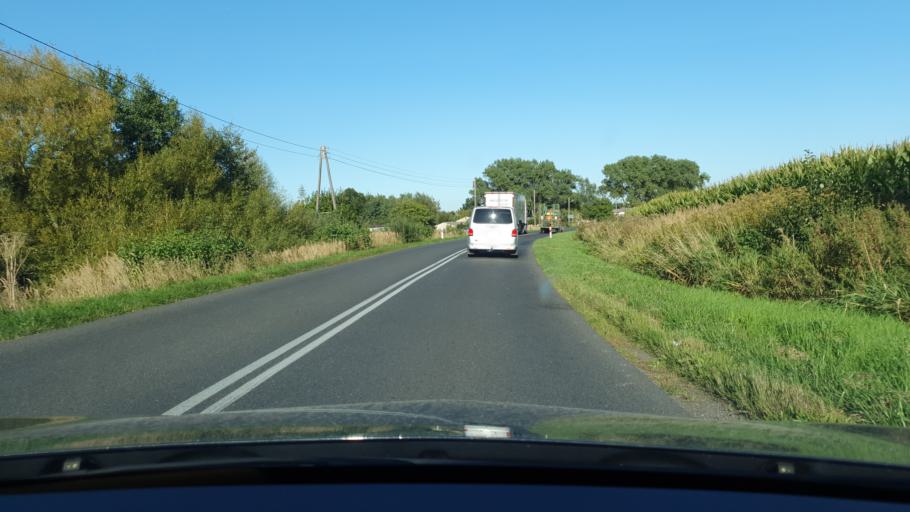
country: PL
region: West Pomeranian Voivodeship
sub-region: Powiat kamienski
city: Golczewo
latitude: 53.8259
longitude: 14.9052
